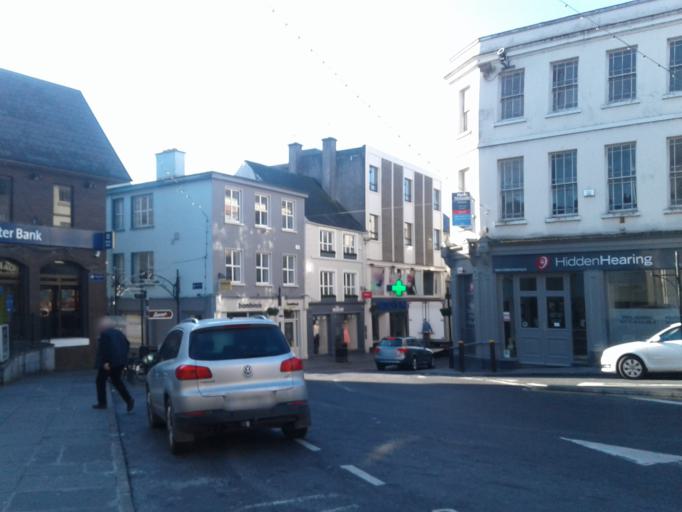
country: IE
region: Munster
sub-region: An Clar
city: Ennis
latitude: 52.8444
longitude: -8.9828
